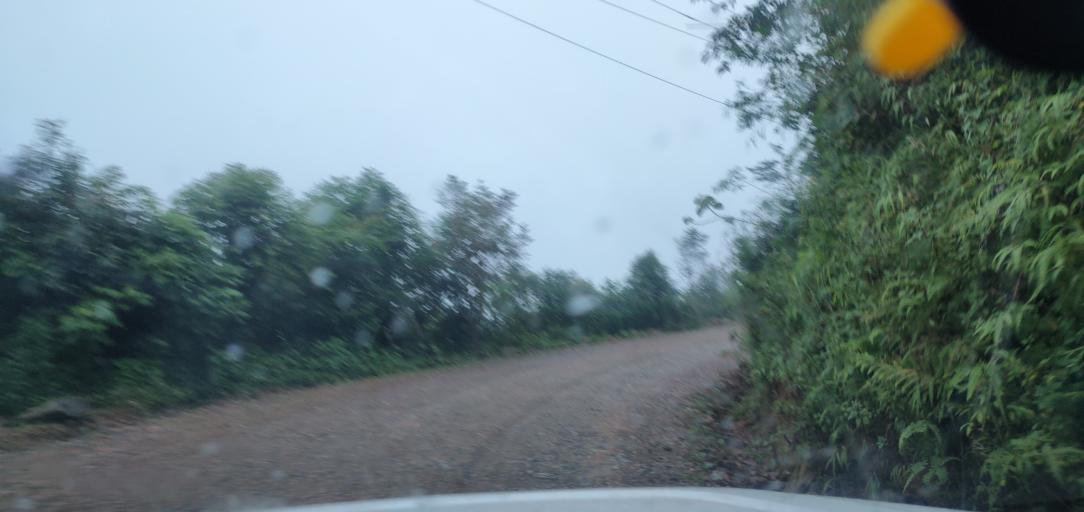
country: LA
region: Phongsali
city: Phongsali
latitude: 21.3963
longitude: 102.1927
